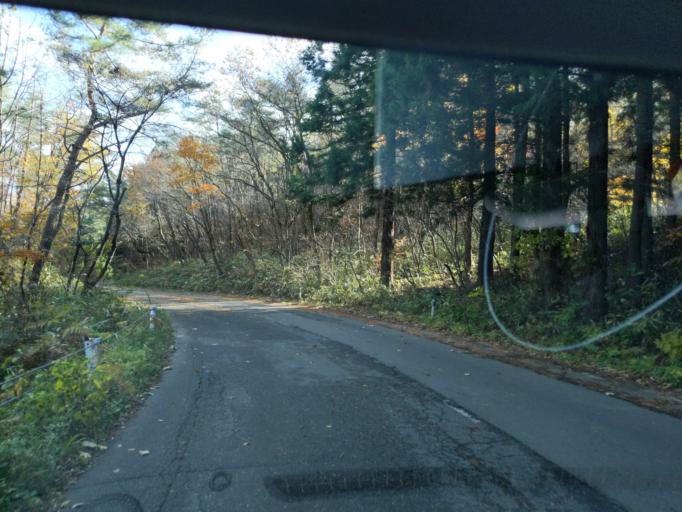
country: JP
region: Iwate
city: Mizusawa
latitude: 39.0430
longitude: 141.0890
